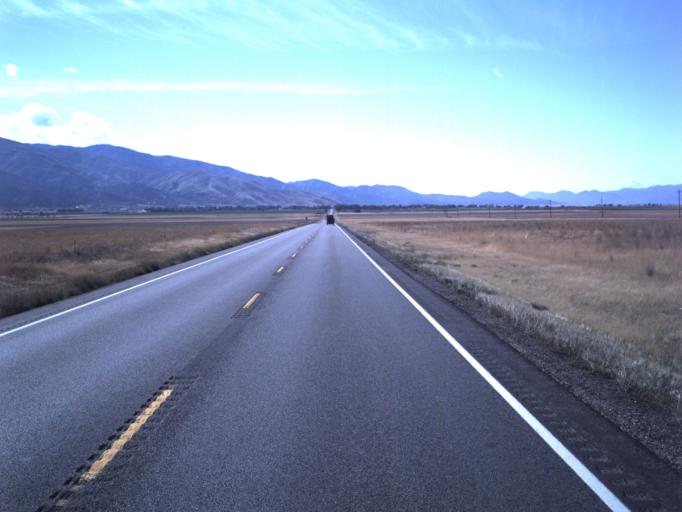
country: US
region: Utah
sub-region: Juab County
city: Nephi
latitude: 39.5986
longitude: -111.8618
